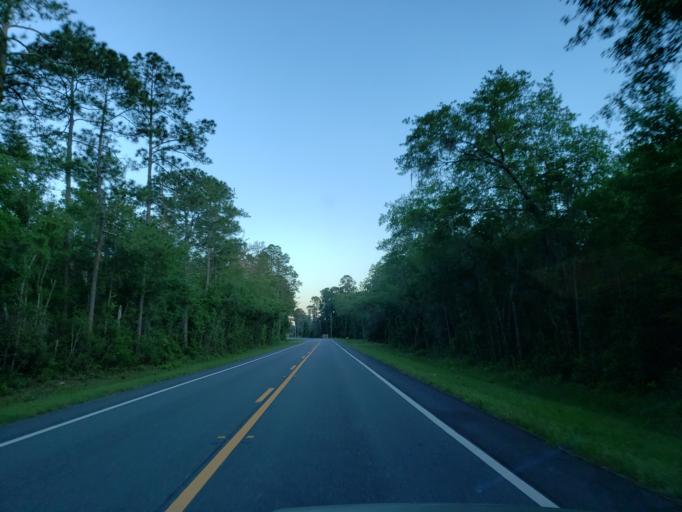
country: US
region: Georgia
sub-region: Echols County
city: Statenville
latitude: 30.5763
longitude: -83.1666
